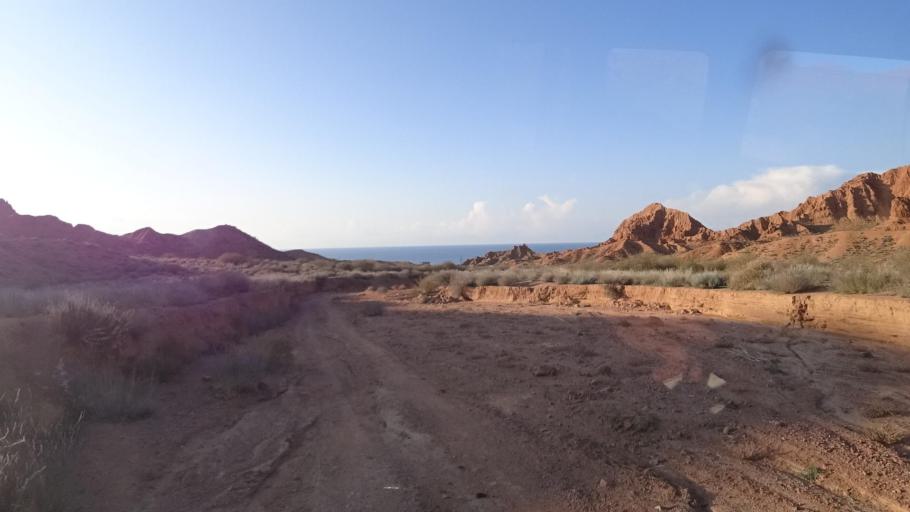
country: KG
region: Ysyk-Koel
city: Kadzhi-Say
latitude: 42.1438
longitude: 77.1490
